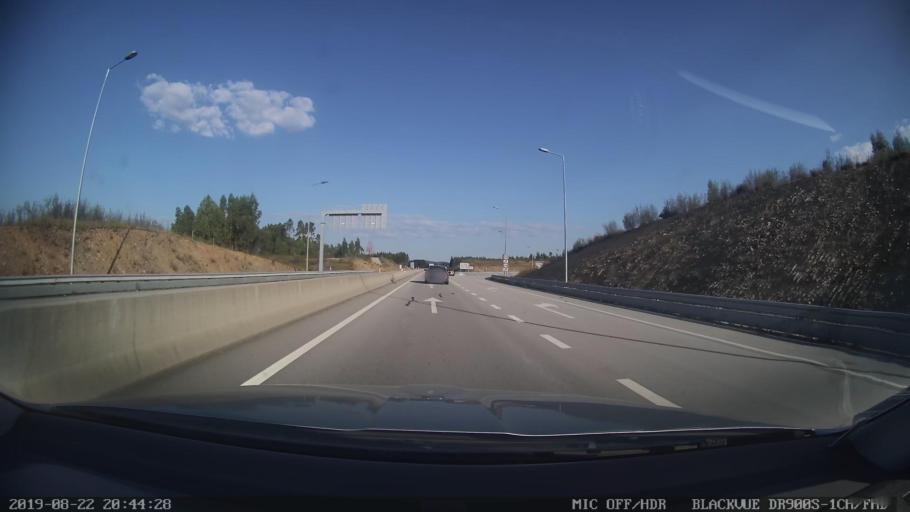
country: PT
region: Castelo Branco
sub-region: Proenca-A-Nova
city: Proenca-a-Nova
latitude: 39.7077
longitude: -7.8520
